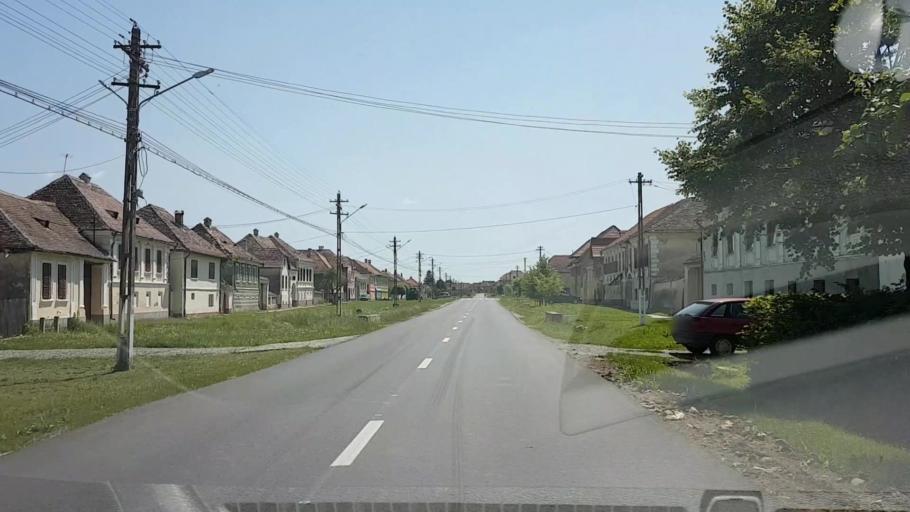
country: RO
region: Sibiu
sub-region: Comuna Merghindeal
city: Merghindeal
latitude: 45.9657
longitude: 24.7257
